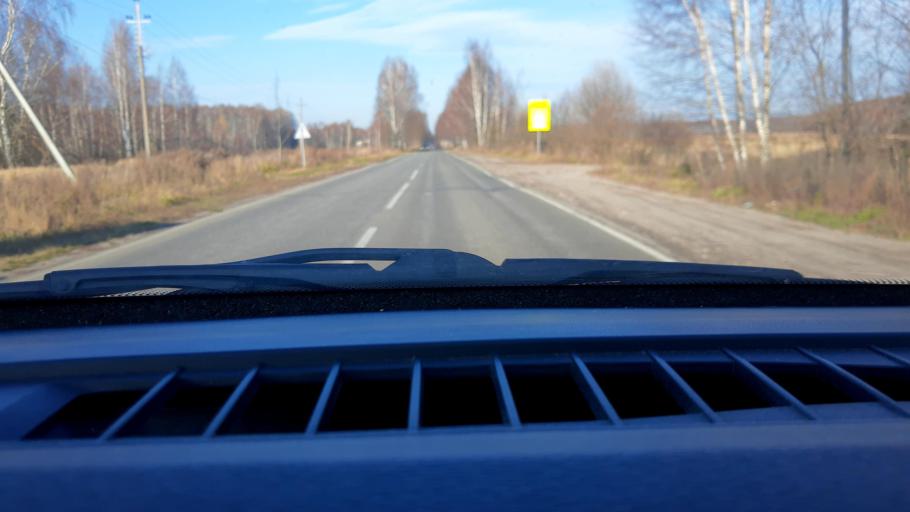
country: RU
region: Nizjnij Novgorod
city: Neklyudovo
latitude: 56.4766
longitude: 43.8749
